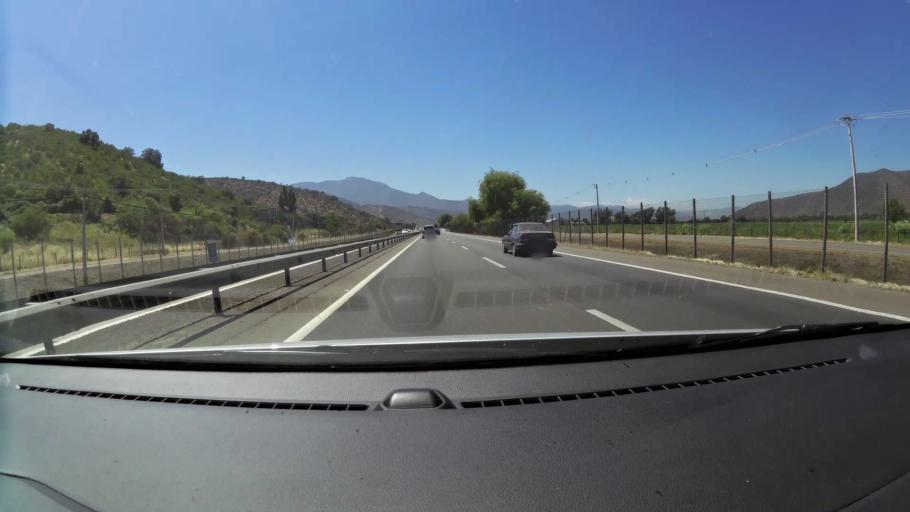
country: CL
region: Santiago Metropolitan
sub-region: Provincia de Chacabuco
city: Lampa
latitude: -33.4042
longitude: -71.0898
